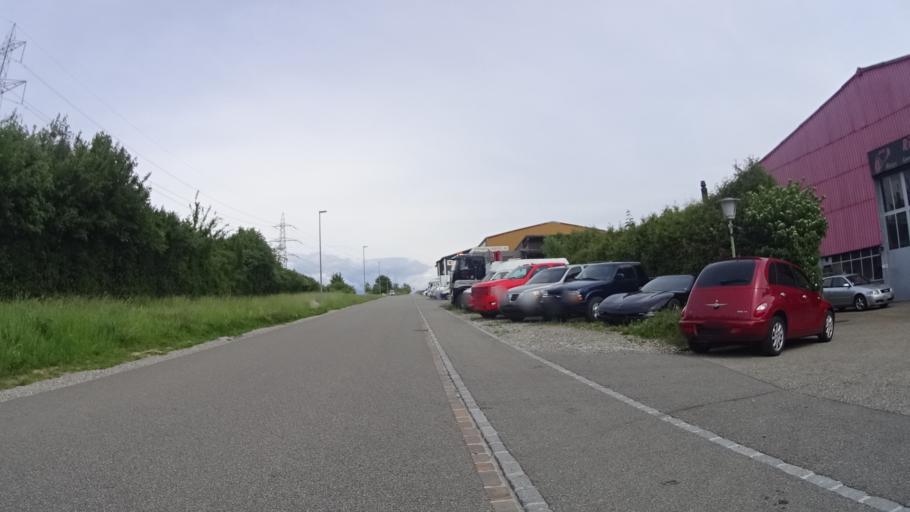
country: CH
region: Aargau
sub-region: Bezirk Rheinfelden
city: Mohlin
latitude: 47.5480
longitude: 7.8744
